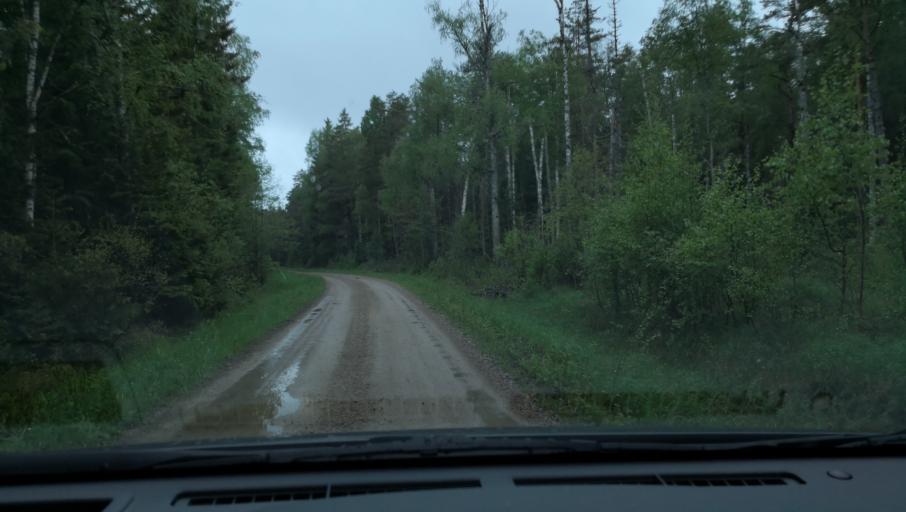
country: SE
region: Uppsala
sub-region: Enkopings Kommun
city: Orsundsbro
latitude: 59.9261
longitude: 17.3360
